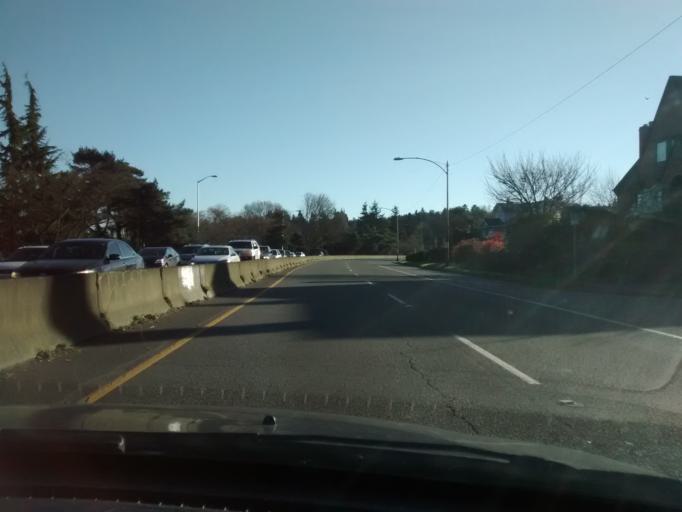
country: US
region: Washington
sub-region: King County
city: Seattle
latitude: 47.6788
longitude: -122.3455
